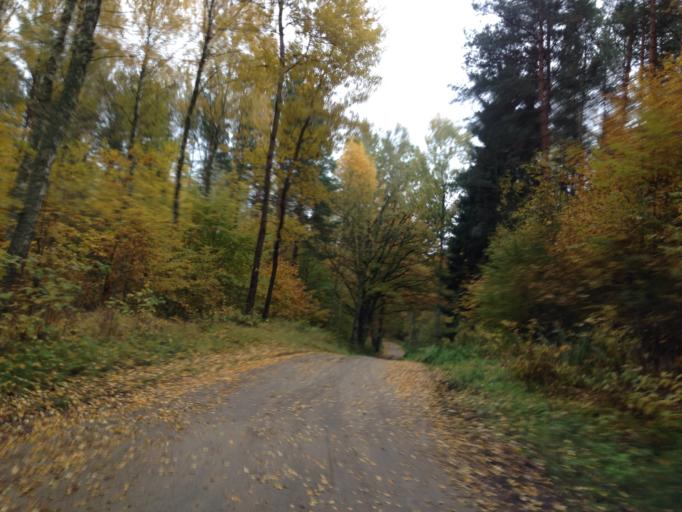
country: PL
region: Pomeranian Voivodeship
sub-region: Powiat kwidzynski
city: Prabuty
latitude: 53.7168
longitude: 19.2323
